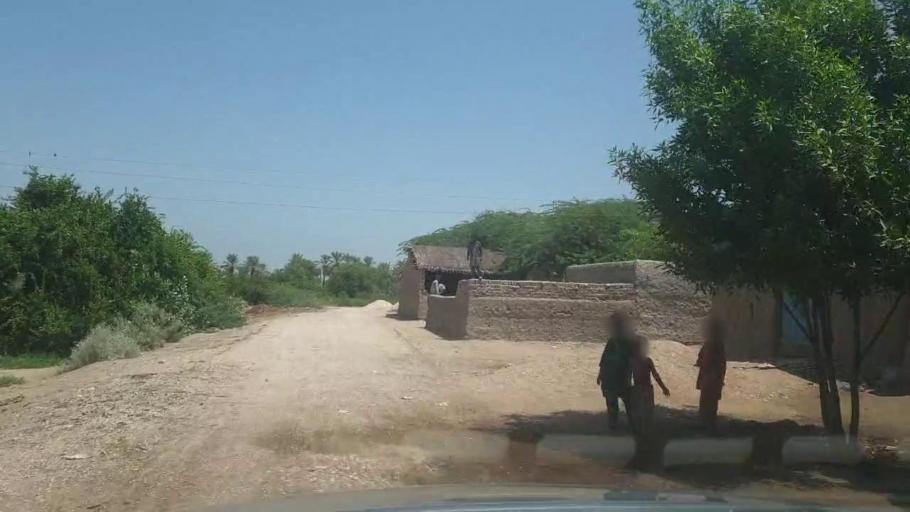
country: PK
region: Sindh
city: Kot Diji
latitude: 27.3309
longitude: 69.0100
